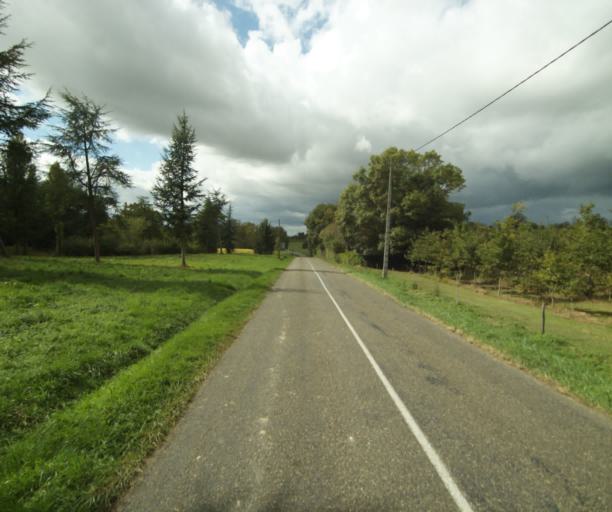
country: FR
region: Midi-Pyrenees
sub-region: Departement du Gers
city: Eauze
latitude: 43.8629
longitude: 0.0248
